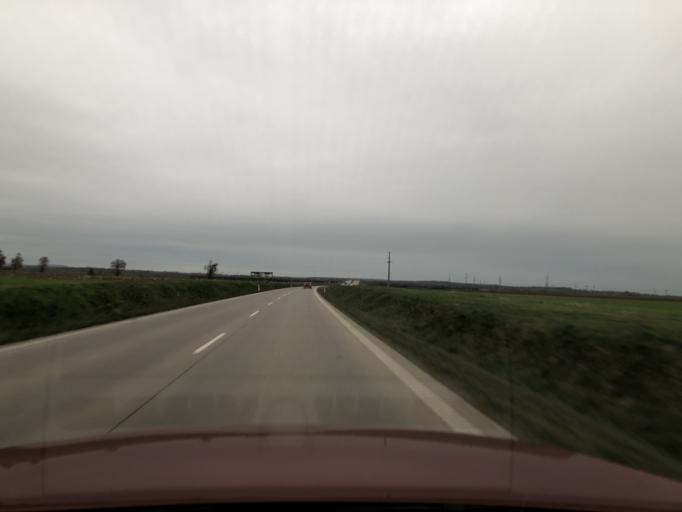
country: PL
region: Lower Silesian Voivodeship
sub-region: Powiat swidnicki
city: Zarow
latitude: 50.9272
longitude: 16.4745
